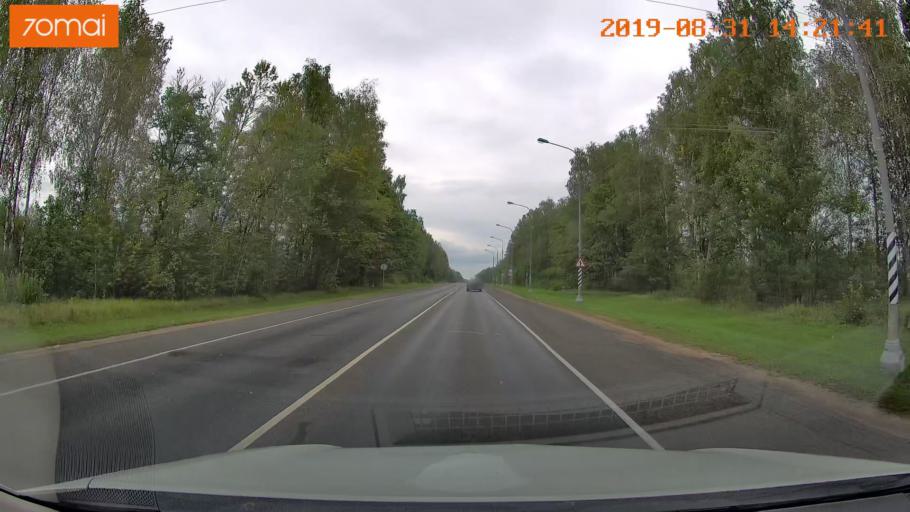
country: RU
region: Smolensk
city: Yekimovichi
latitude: 54.0870
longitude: 33.2025
